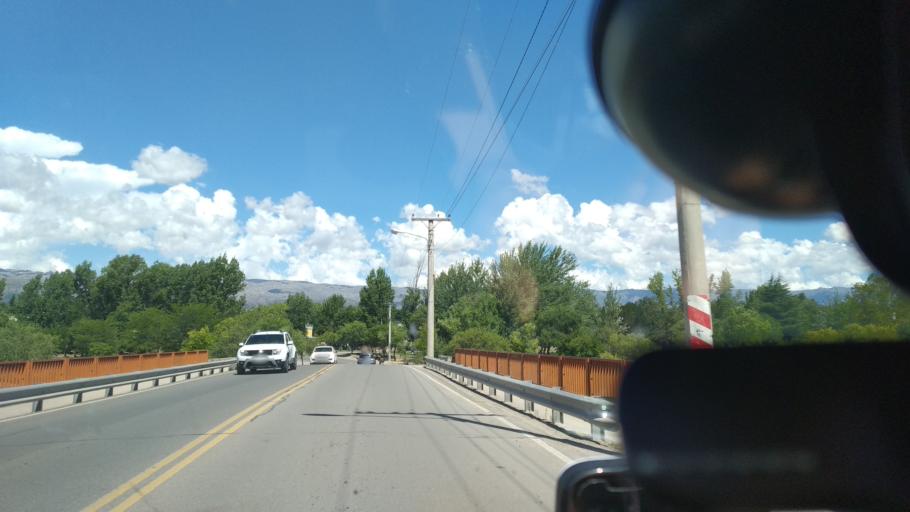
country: AR
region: Cordoba
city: Mina Clavero
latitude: -31.7195
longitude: -65.0093
